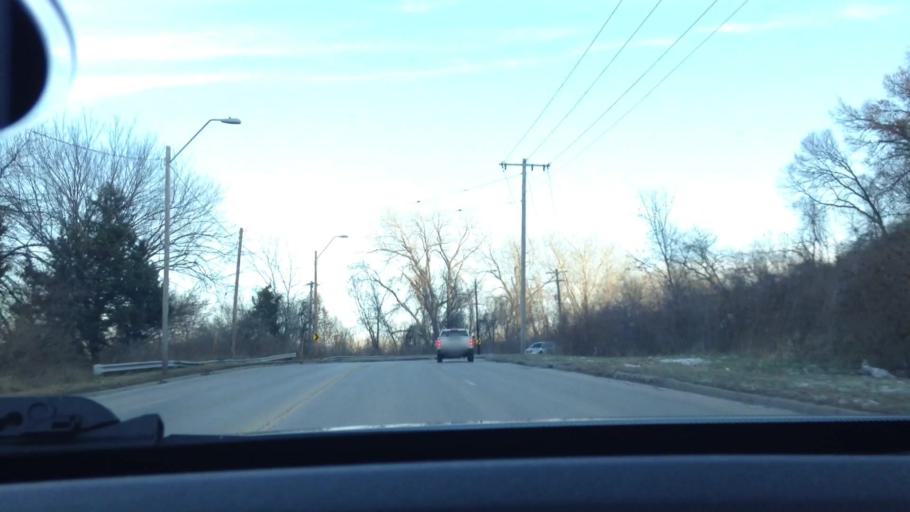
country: US
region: Missouri
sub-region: Clay County
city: North Kansas City
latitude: 39.1200
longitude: -94.5090
